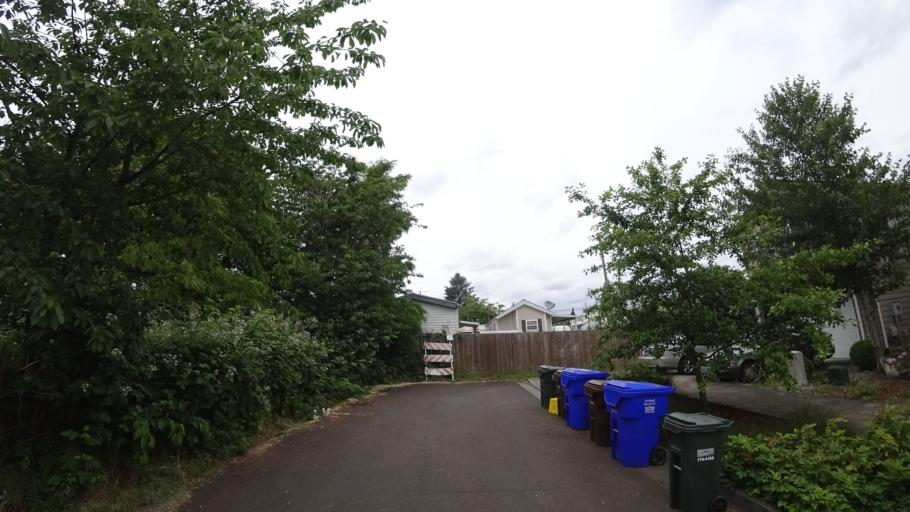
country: US
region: Oregon
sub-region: Multnomah County
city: Lents
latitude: 45.4658
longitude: -122.5812
